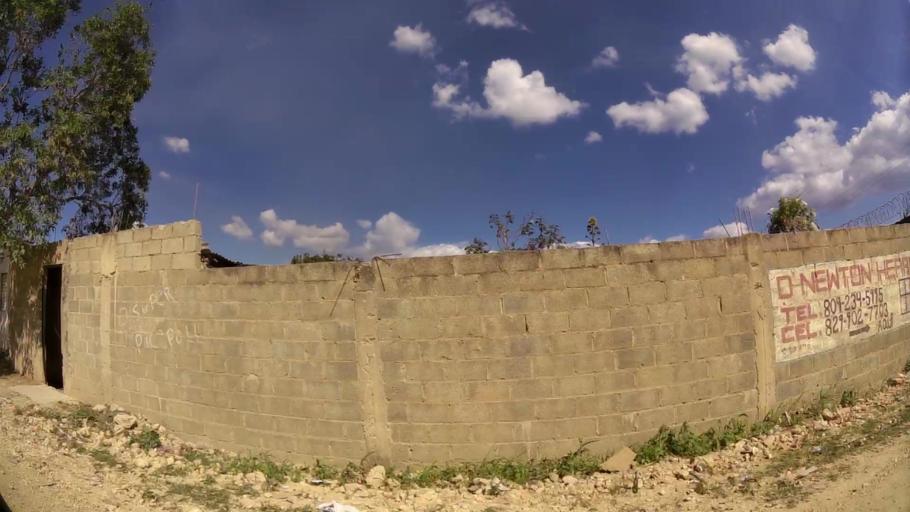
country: DO
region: Santo Domingo
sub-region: Santo Domingo
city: Santo Domingo Este
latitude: 18.4699
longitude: -69.7671
